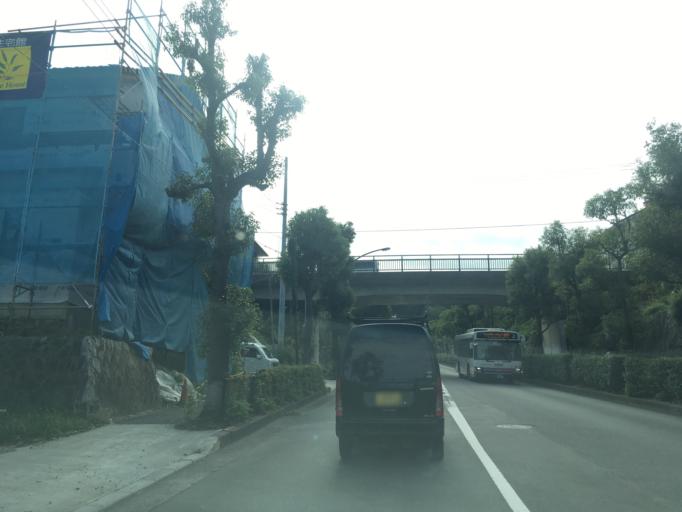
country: JP
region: Tokyo
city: Hino
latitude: 35.6446
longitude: 139.3862
